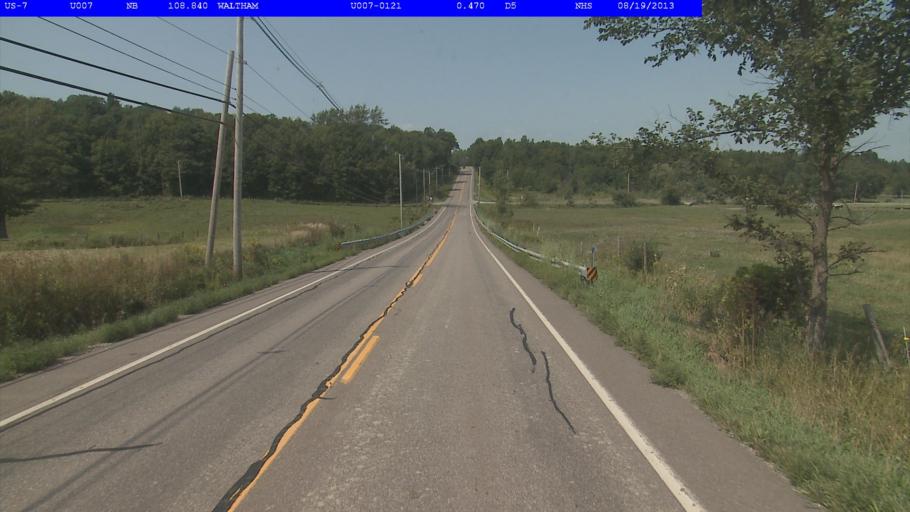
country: US
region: Vermont
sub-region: Addison County
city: Vergennes
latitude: 44.1527
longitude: -73.2165
